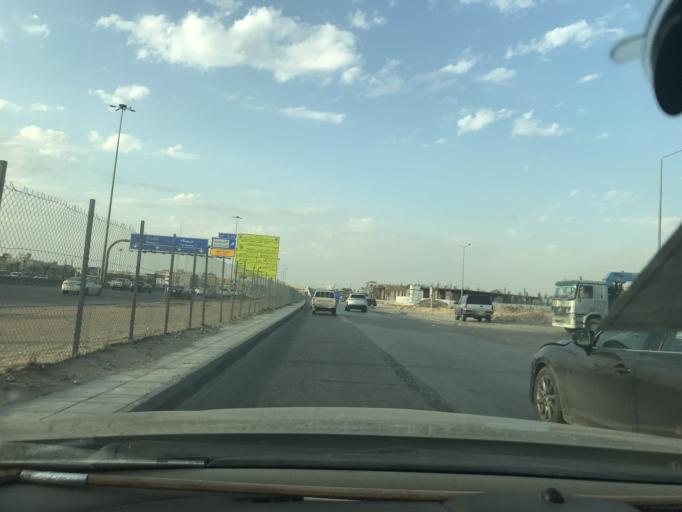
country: SA
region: Ar Riyad
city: Riyadh
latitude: 24.7474
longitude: 46.5850
